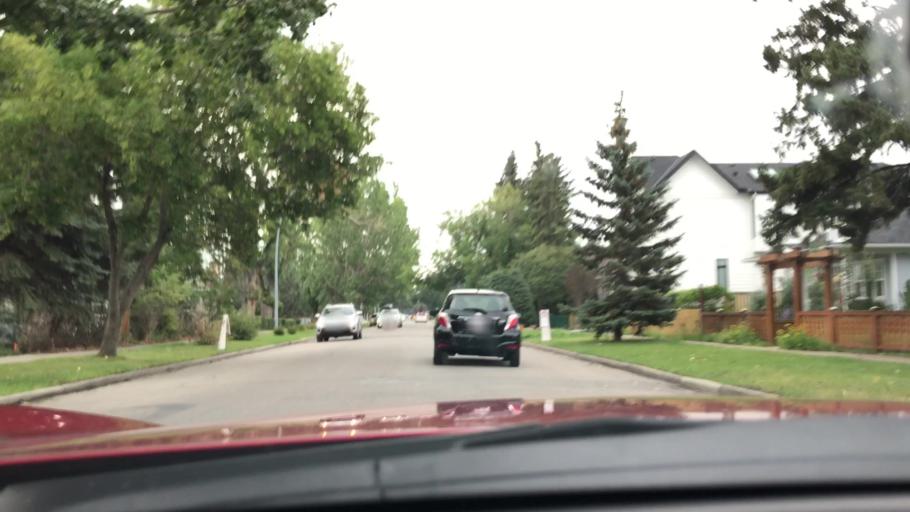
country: CA
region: Alberta
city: Calgary
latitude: 51.0429
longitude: -114.0361
